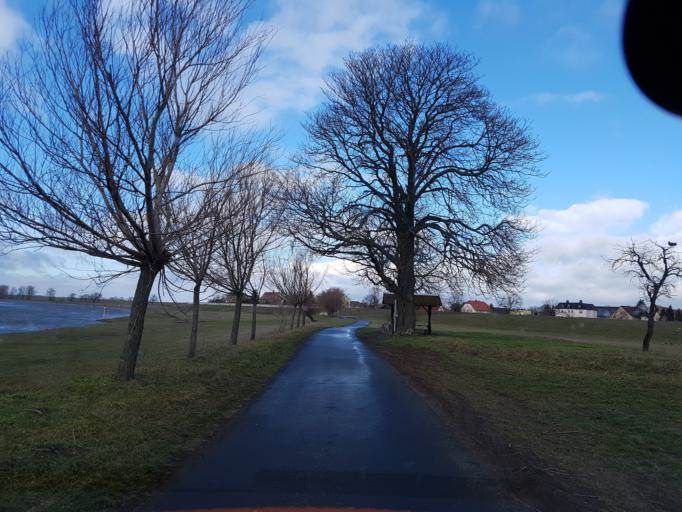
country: DE
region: Saxony
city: Belgern
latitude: 51.4906
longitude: 13.1864
